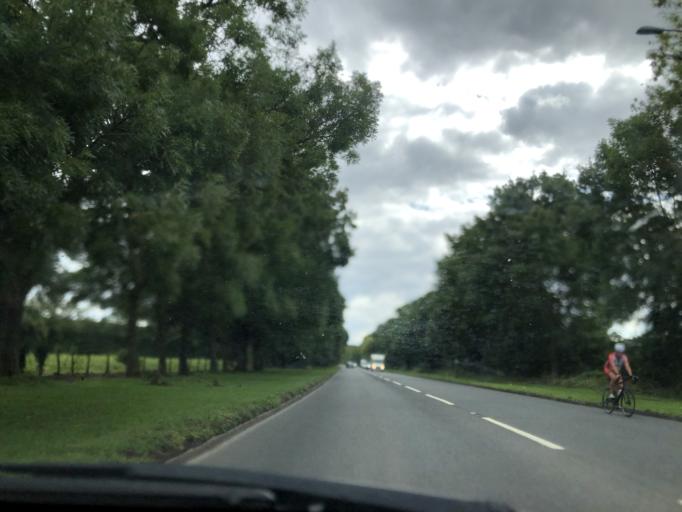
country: GB
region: England
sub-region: Kent
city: Halstead
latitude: 51.3491
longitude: 0.1317
